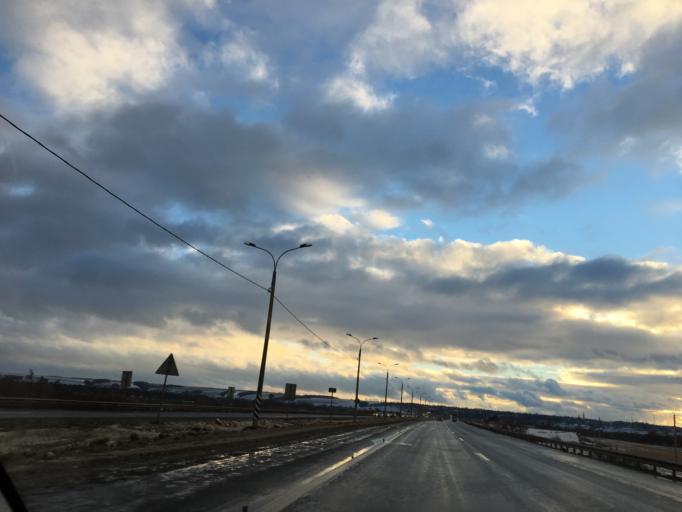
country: RU
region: Moskovskaya
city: Danki
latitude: 54.8797
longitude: 37.5090
